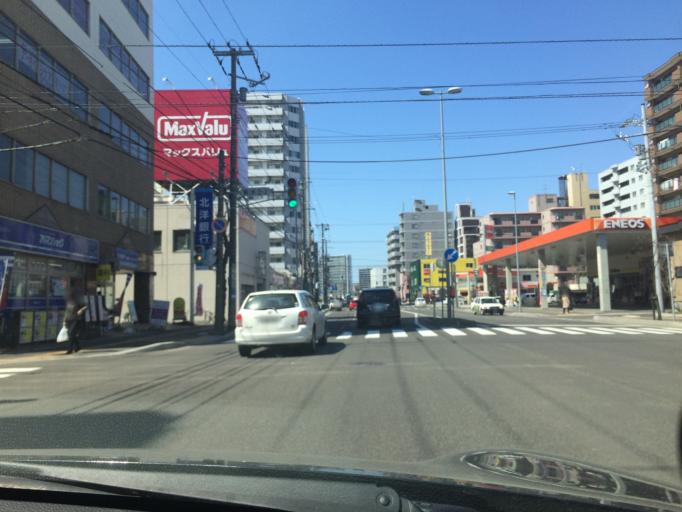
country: JP
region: Hokkaido
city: Sapporo
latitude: 43.0573
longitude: 141.3727
